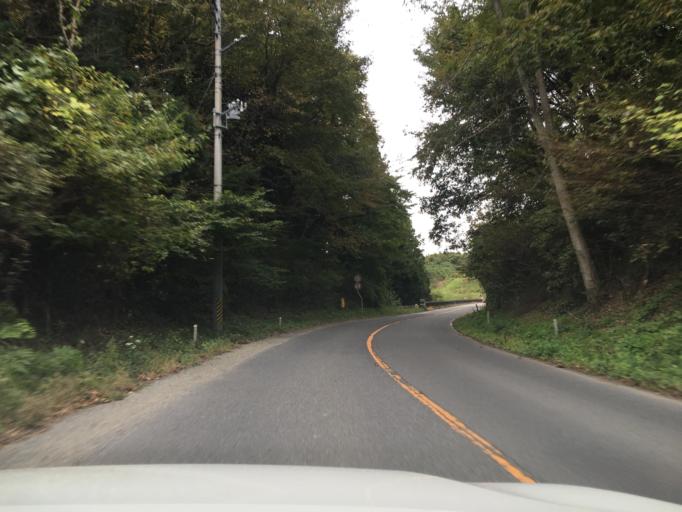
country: JP
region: Fukushima
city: Miharu
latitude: 37.4545
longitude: 140.5062
